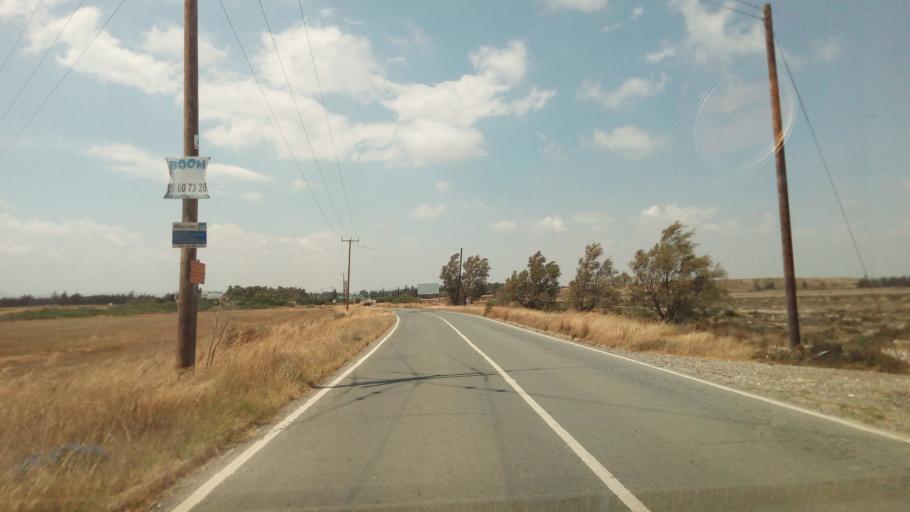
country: CY
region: Larnaka
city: Meneou
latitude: 34.8497
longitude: 33.6119
